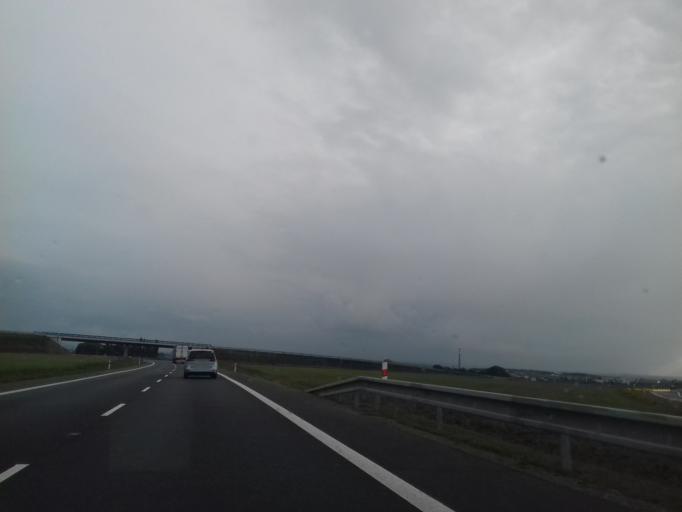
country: CZ
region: Pardubicky
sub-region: Okres Chrudim
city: Chrudim
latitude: 49.9781
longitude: 15.7806
